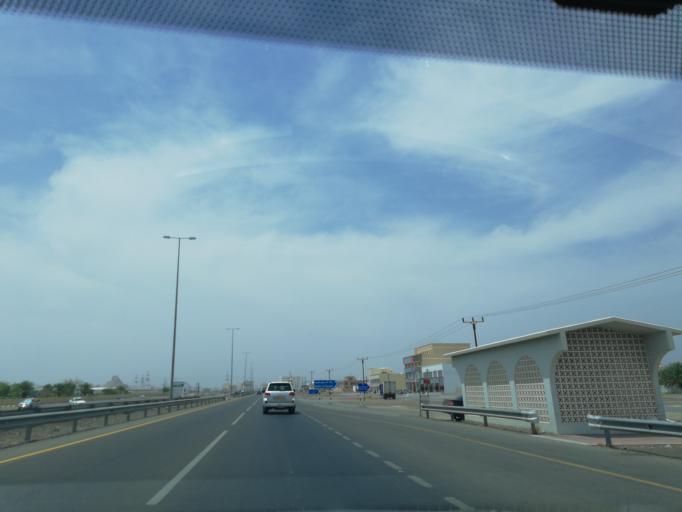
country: OM
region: Muhafazat ad Dakhiliyah
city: Nizwa
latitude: 22.8580
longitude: 57.5223
